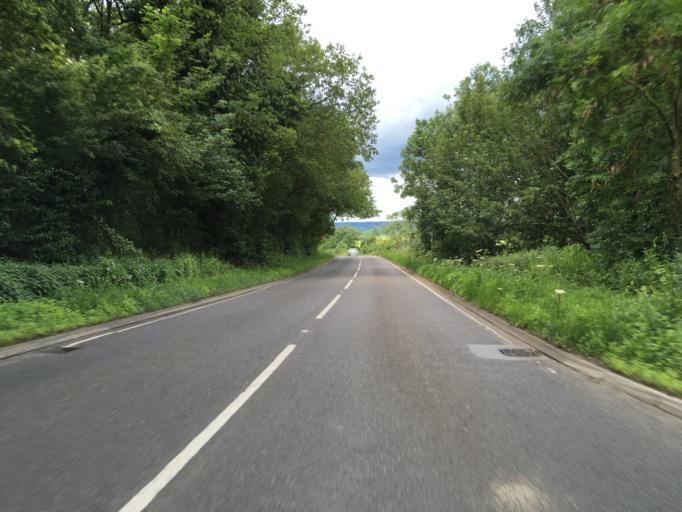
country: GB
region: England
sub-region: Oxfordshire
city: Adderbury
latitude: 52.0926
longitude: -1.2393
